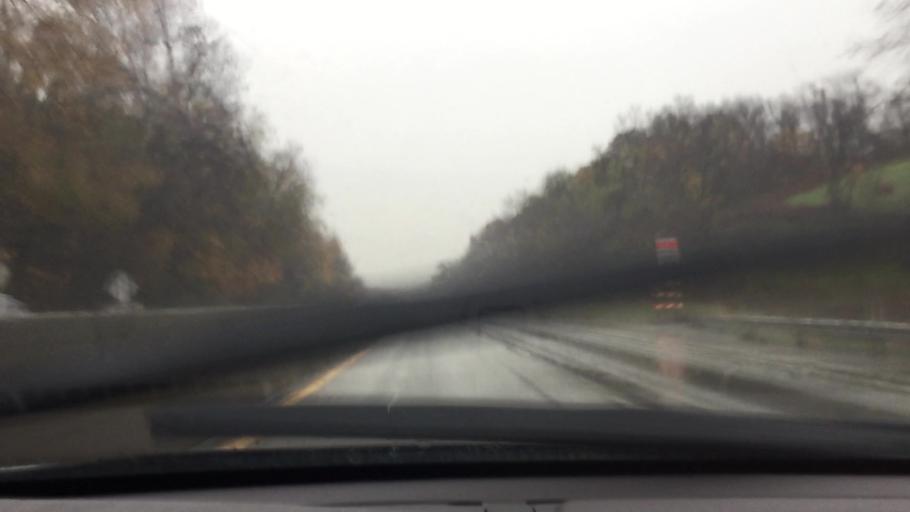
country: US
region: Pennsylvania
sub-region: Washington County
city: East Washington
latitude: 40.1625
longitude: -80.1618
